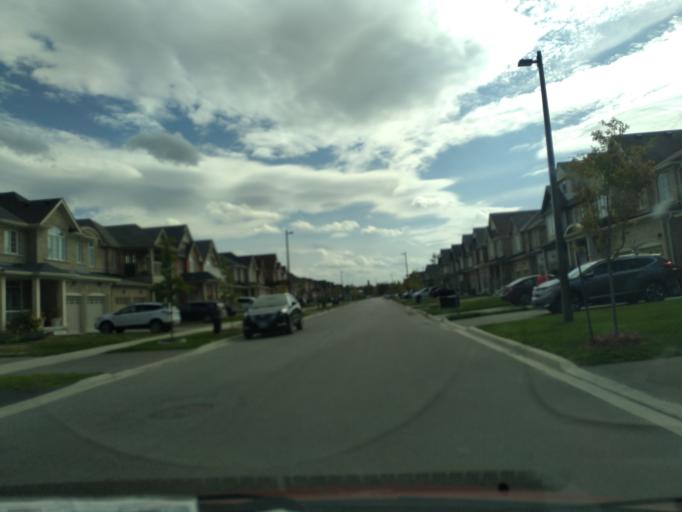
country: CA
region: Ontario
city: Keswick
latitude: 44.3053
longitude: -79.3773
